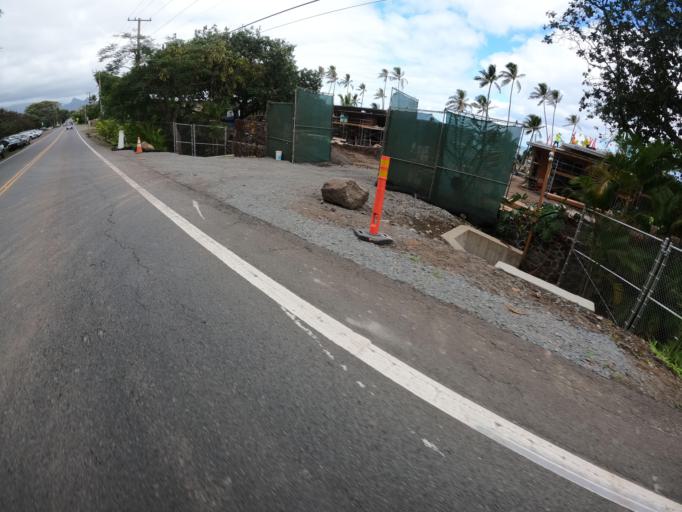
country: US
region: Hawaii
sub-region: Honolulu County
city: Waimanalo Beach
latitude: 21.3245
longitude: -157.6801
